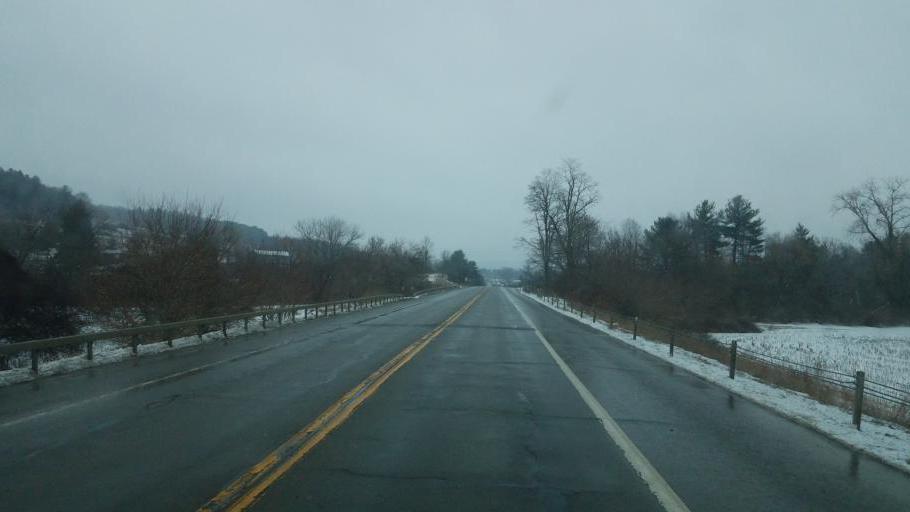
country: US
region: Pennsylvania
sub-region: Tioga County
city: Elkland
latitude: 42.0906
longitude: -77.4189
